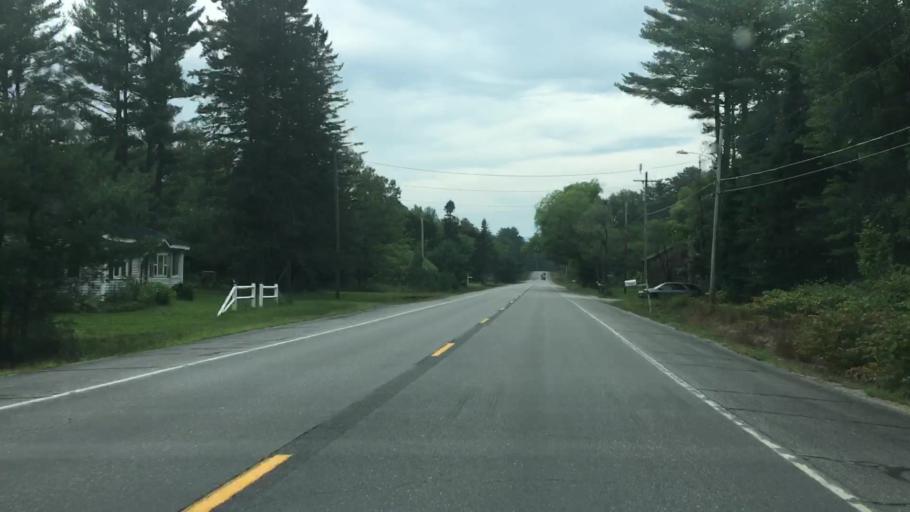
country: US
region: Maine
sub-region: Oxford County
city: Bethel
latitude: 44.4853
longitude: -70.7173
